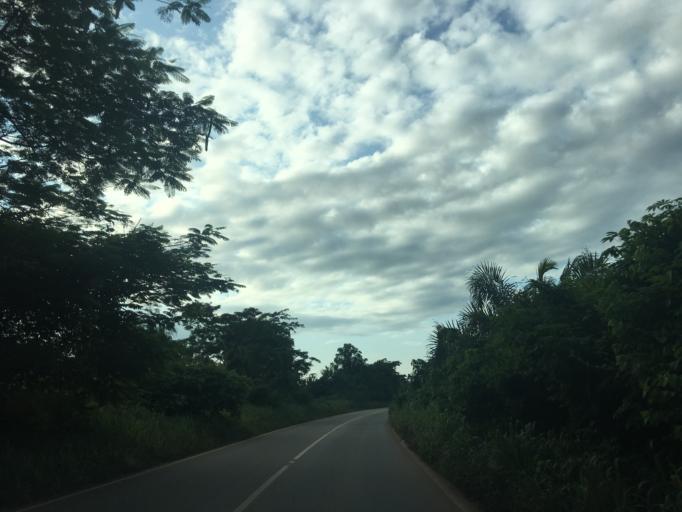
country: GH
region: Western
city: Bibiani
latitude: 6.3684
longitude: -2.2894
